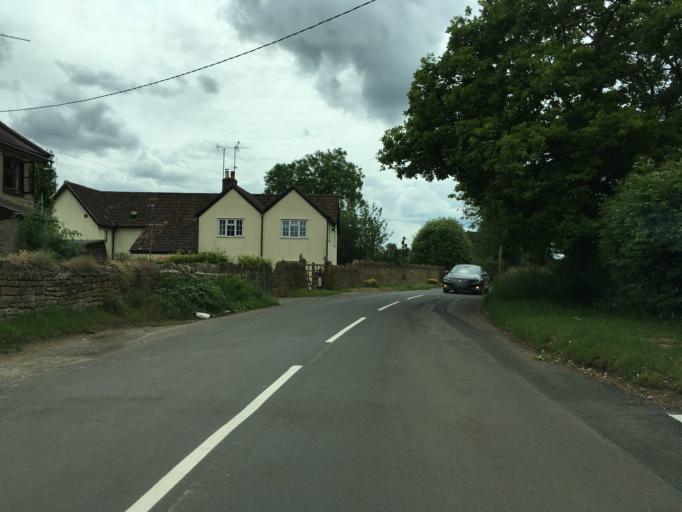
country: GB
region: England
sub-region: Wiltshire
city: Charlton
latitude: 51.5425
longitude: -2.0540
